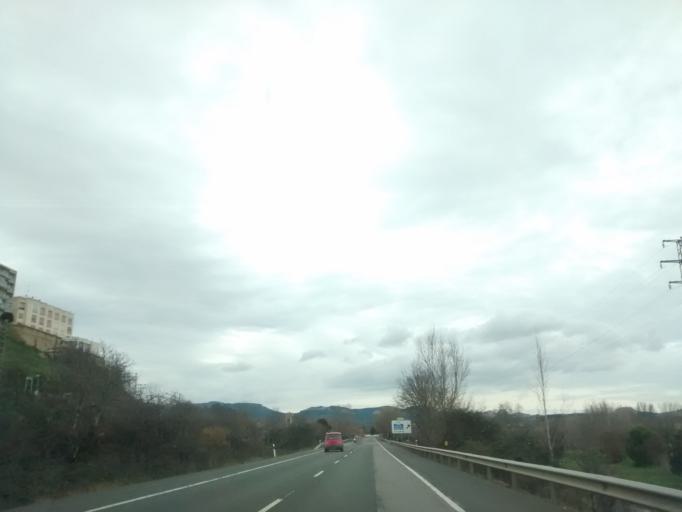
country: ES
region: La Rioja
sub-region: Provincia de La Rioja
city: Haro
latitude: 42.5769
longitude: -2.8420
